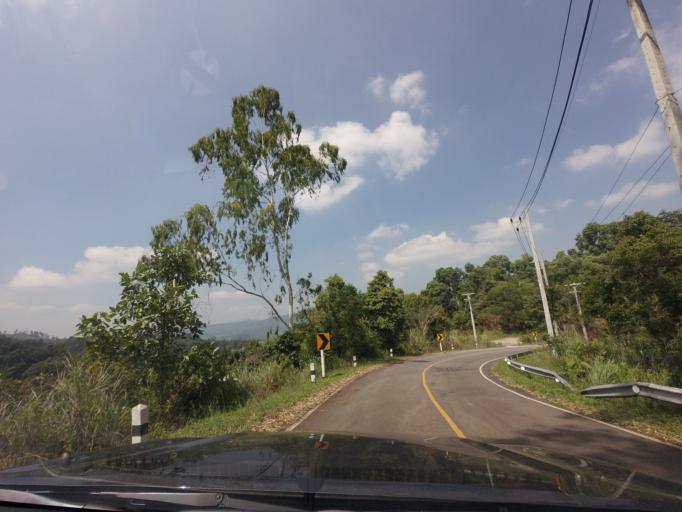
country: TH
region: Loei
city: Na Haeo
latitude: 17.4895
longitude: 100.9019
